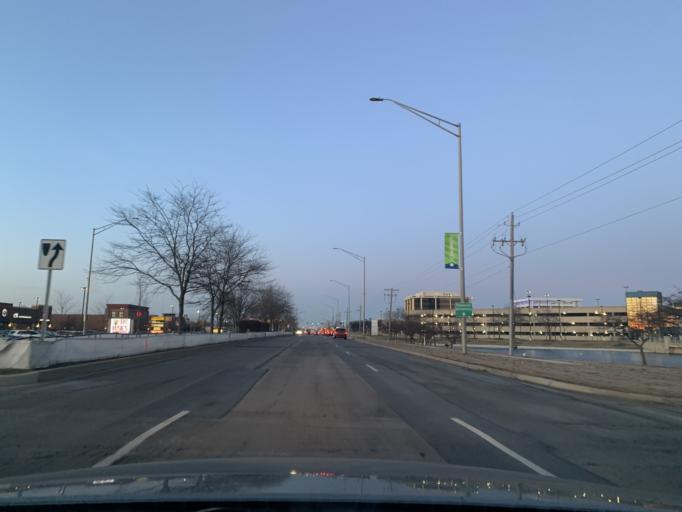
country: US
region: Illinois
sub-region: Cook County
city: Hoffman Estates
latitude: 42.0447
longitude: -88.0452
